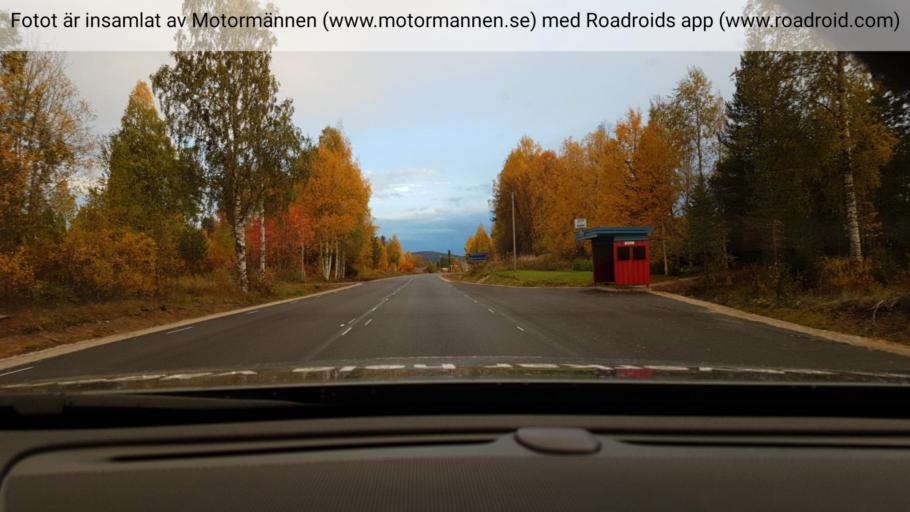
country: SE
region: Norrbotten
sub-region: Overkalix Kommun
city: OEverkalix
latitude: 66.3710
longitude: 22.8428
